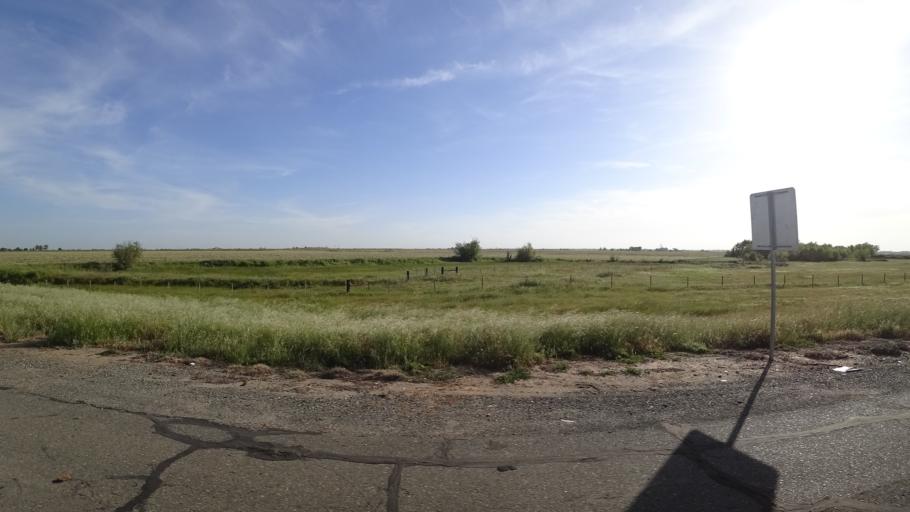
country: US
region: California
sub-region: Yuba County
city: Olivehurst
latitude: 39.0566
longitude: -121.5021
